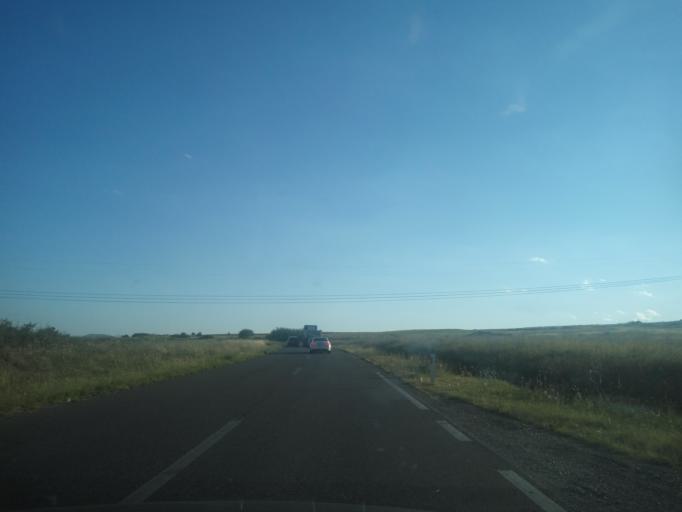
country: XK
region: Gjakova
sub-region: Komuna e Gjakoves
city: Gjakove
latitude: 42.4489
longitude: 20.4951
